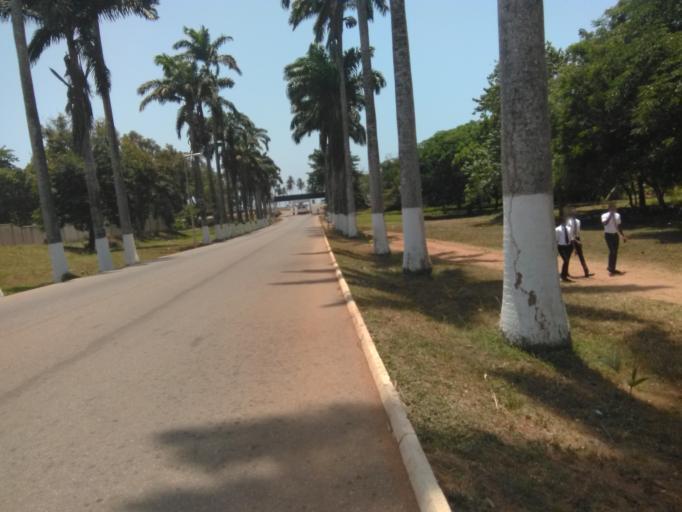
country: GH
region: Central
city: Cape Coast
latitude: 5.1030
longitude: -1.2843
